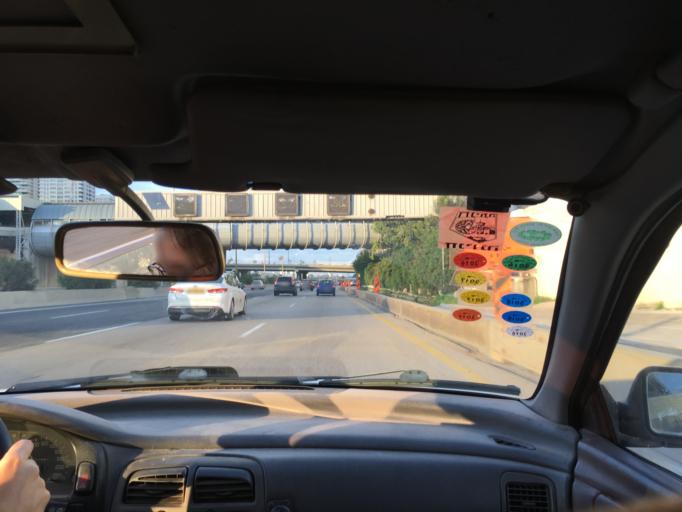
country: IL
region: Tel Aviv
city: Ramat Gan
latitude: 32.0828
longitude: 34.7986
